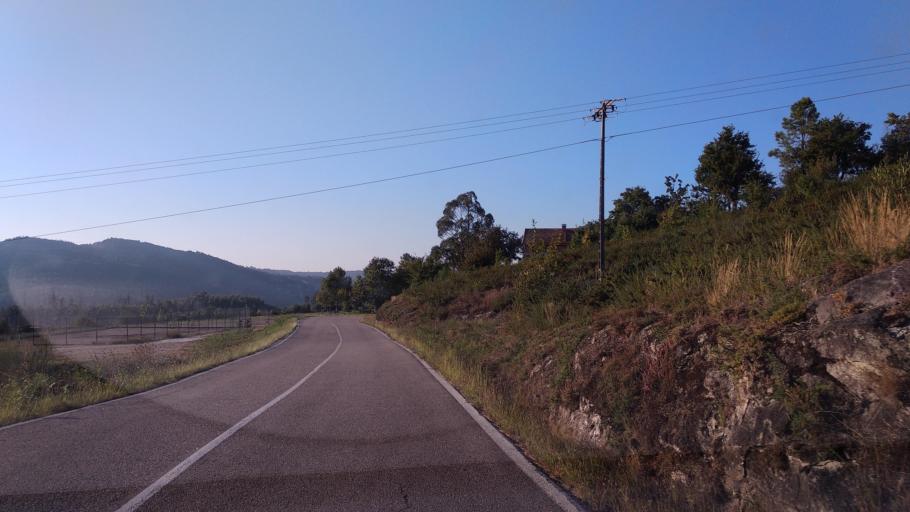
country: ES
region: Galicia
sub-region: Provincia de Pontevedra
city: Ponte Caldelas
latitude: 42.3585
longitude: -8.5305
